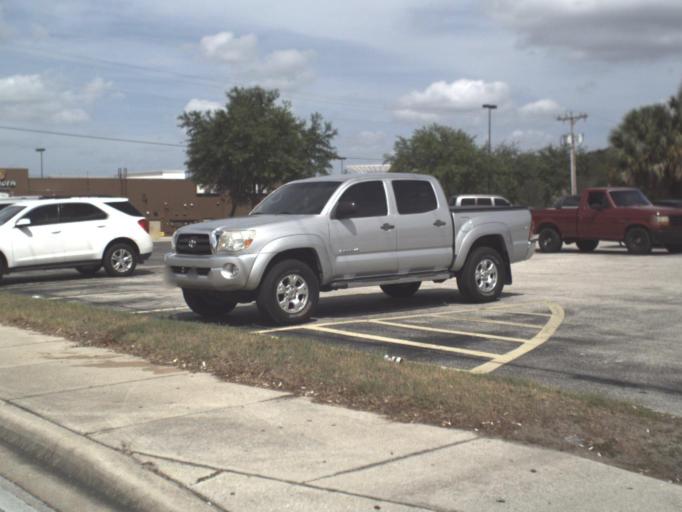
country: US
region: Florida
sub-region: Clay County
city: Lakeside
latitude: 30.1480
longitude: -81.7569
